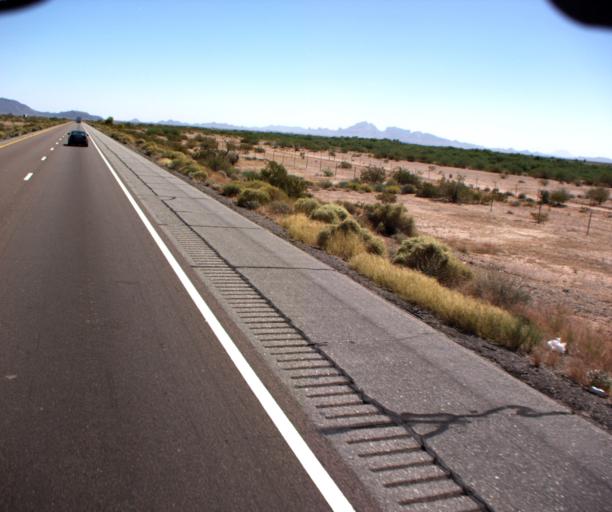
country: US
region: Arizona
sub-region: La Paz County
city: Salome
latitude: 33.5479
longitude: -113.2163
